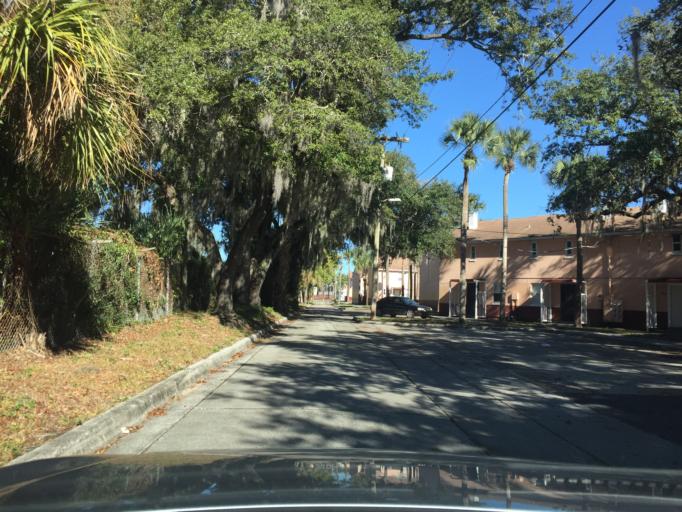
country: US
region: Florida
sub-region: Hillsborough County
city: Tampa
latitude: 27.9763
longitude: -82.4573
